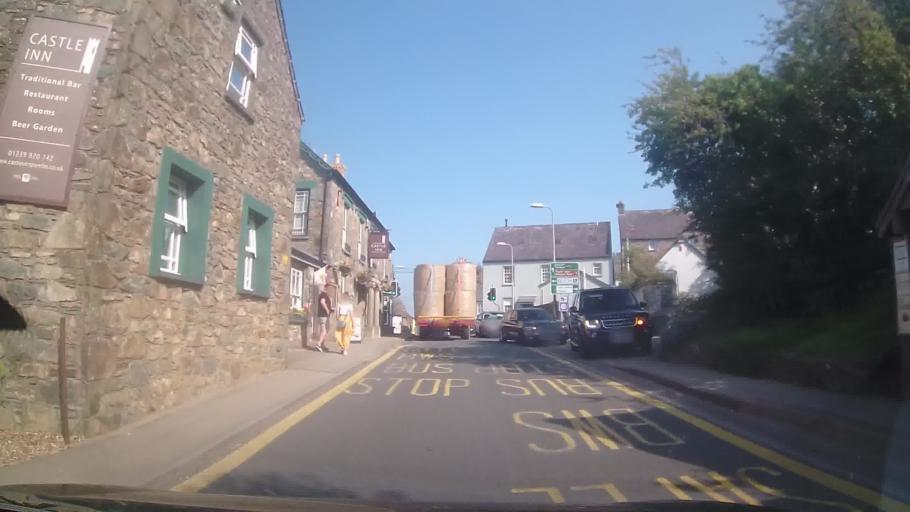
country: GB
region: Wales
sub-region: Pembrokeshire
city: Newport
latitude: 52.0161
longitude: -4.8338
